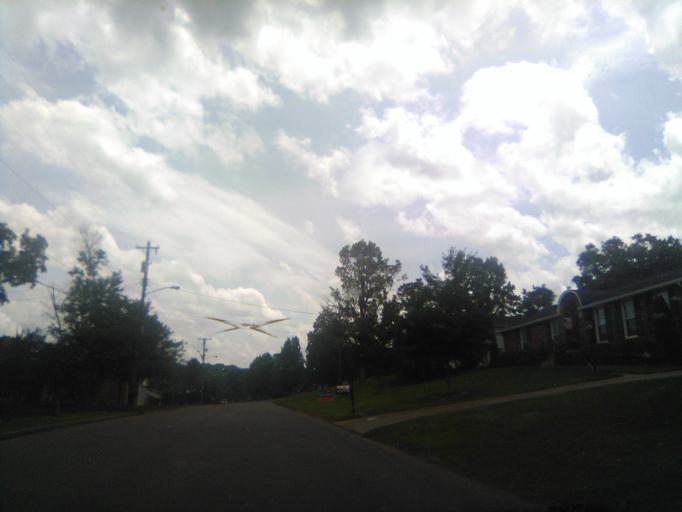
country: US
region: Tennessee
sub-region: Davidson County
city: Belle Meade
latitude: 36.0889
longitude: -86.8843
